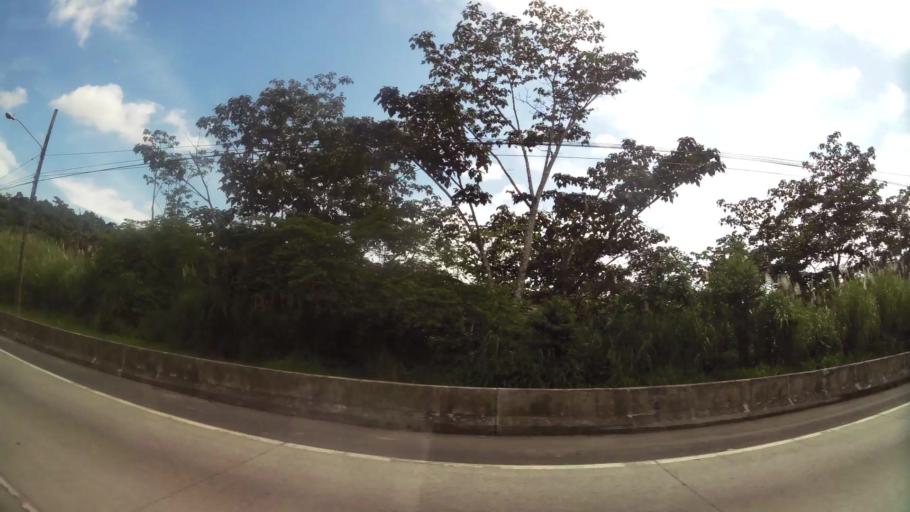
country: PA
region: Panama
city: Las Cumbres
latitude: 9.0398
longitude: -79.5516
